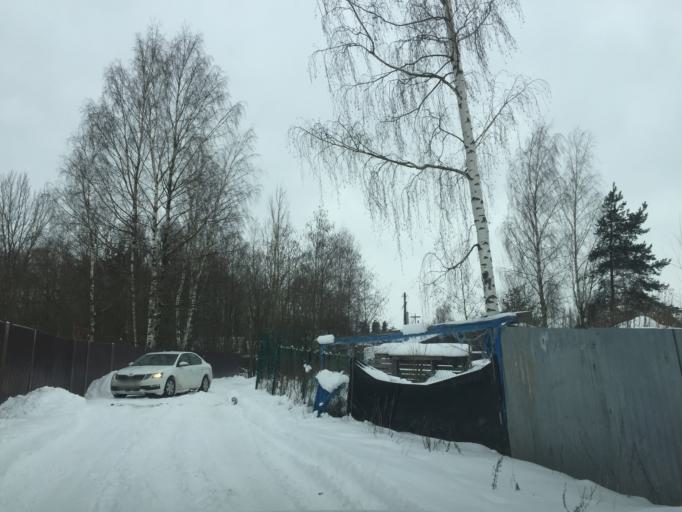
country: RU
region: Leningrad
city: Otradnoye
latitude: 59.7822
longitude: 30.7873
